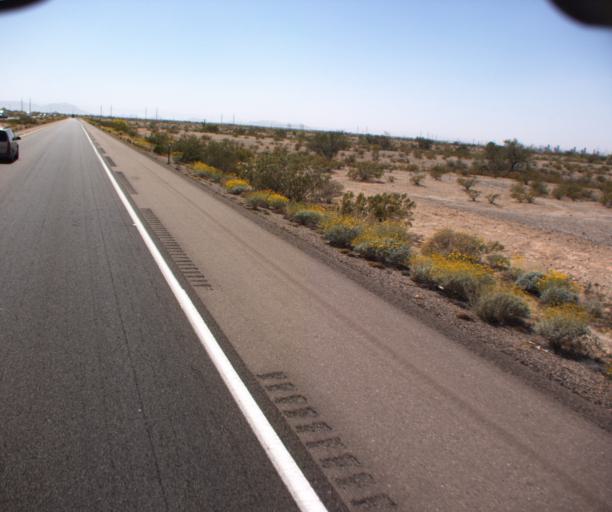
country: US
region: Arizona
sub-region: Maricopa County
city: Gila Bend
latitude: 32.9852
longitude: -112.6665
